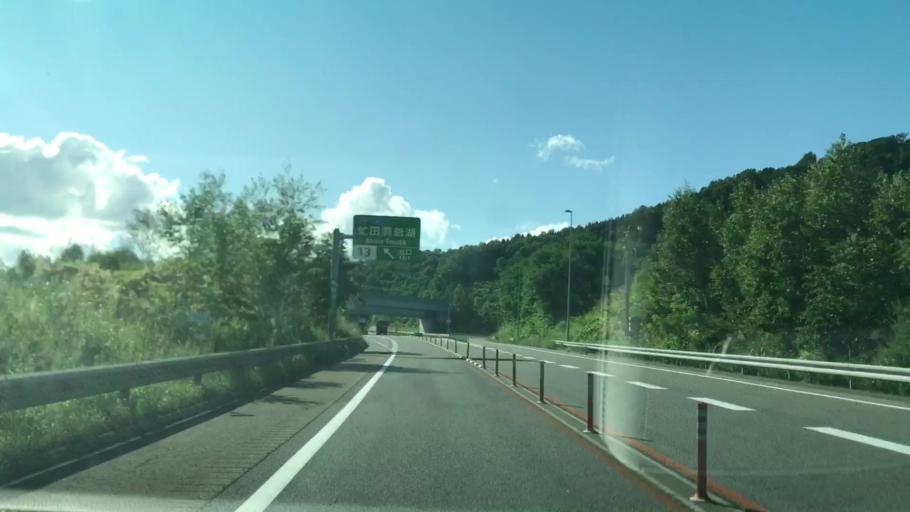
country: JP
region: Hokkaido
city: Date
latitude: 42.5579
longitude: 140.7747
